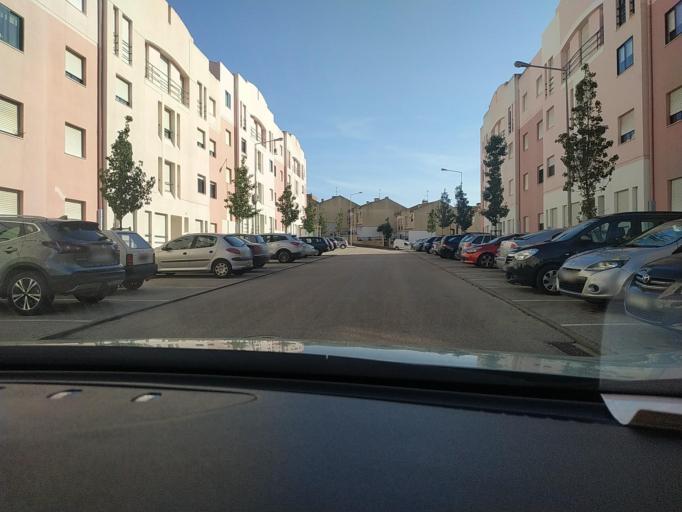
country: PT
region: Lisbon
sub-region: Loures
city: Apelacao
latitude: 38.8237
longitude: -9.1438
